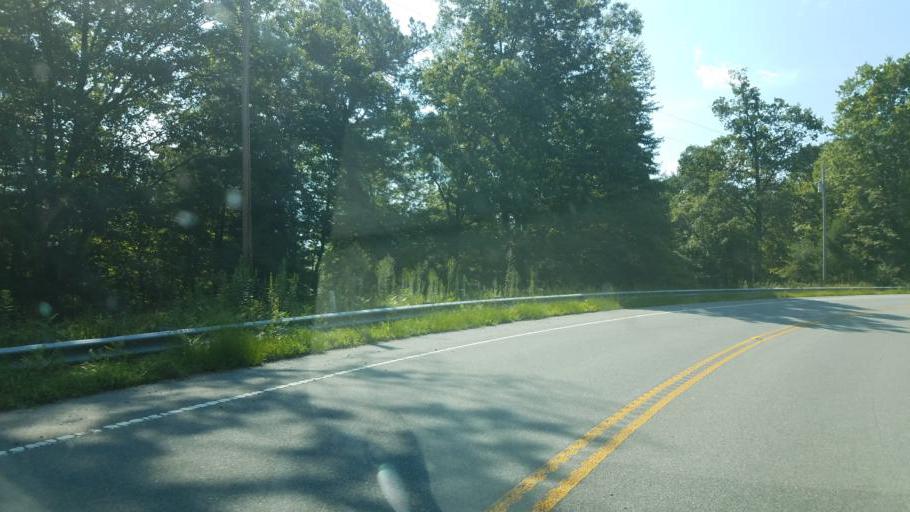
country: US
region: North Carolina
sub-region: Burke County
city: Glen Alpine
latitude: 35.9141
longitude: -81.8102
